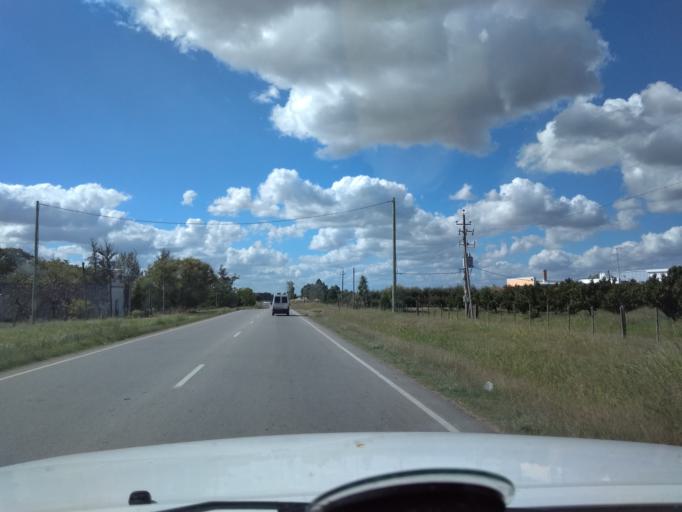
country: UY
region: Canelones
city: Sauce
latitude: -34.6833
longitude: -56.0528
